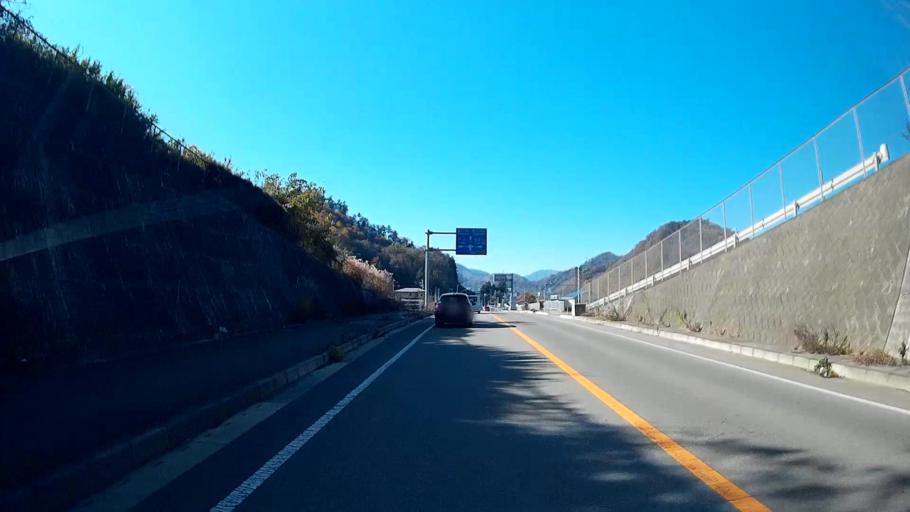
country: JP
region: Yamanashi
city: Otsuki
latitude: 35.5536
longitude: 138.9327
